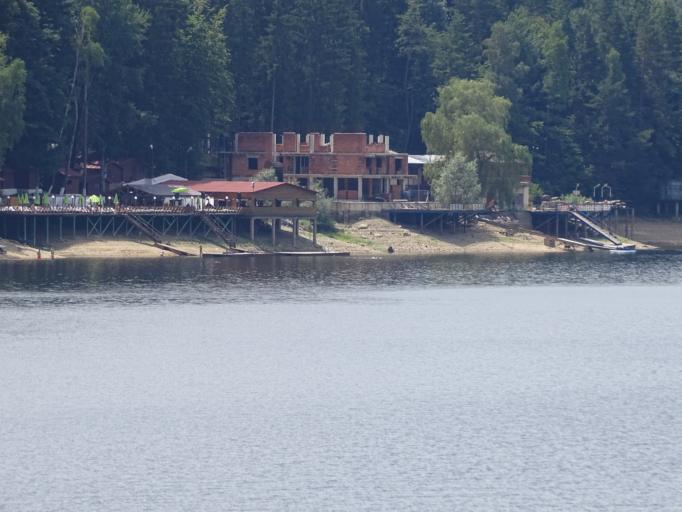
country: RO
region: Caras-Severin
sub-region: Comuna Valiug
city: Valiug
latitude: 45.2167
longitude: 22.0266
